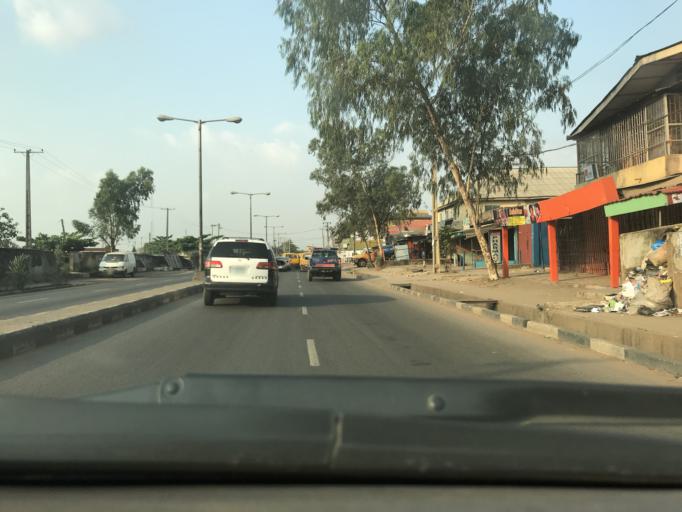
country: NG
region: Lagos
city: Agege
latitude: 6.6081
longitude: 3.2941
